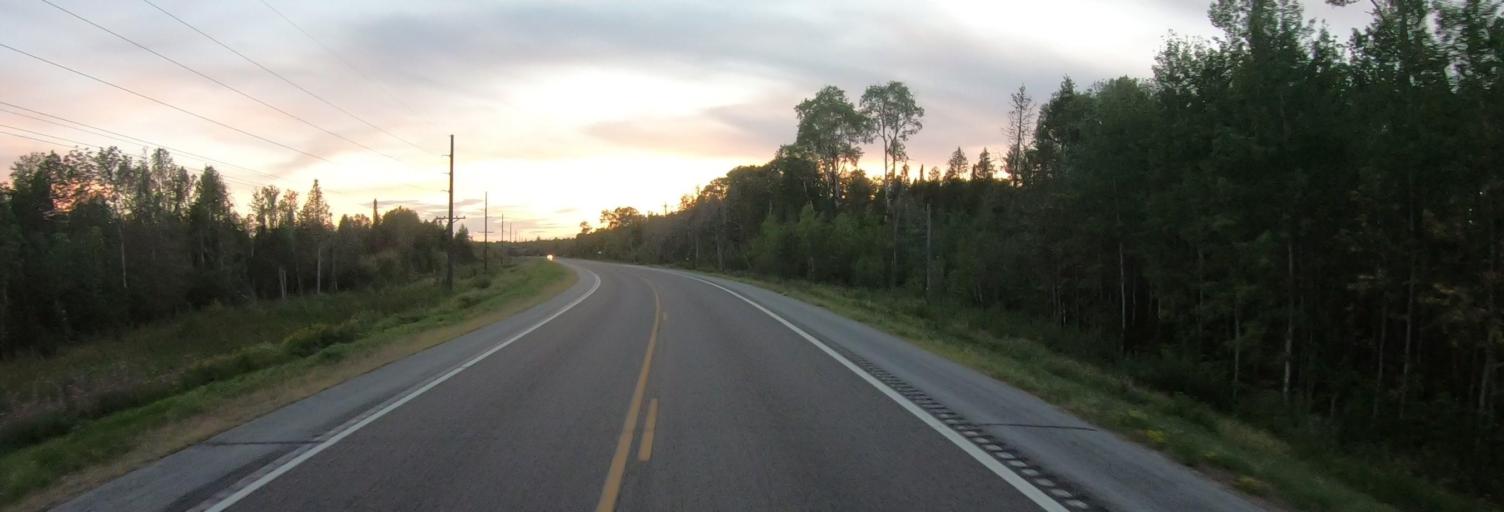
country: US
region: Minnesota
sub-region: Saint Louis County
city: Virginia
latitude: 47.8561
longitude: -92.4732
